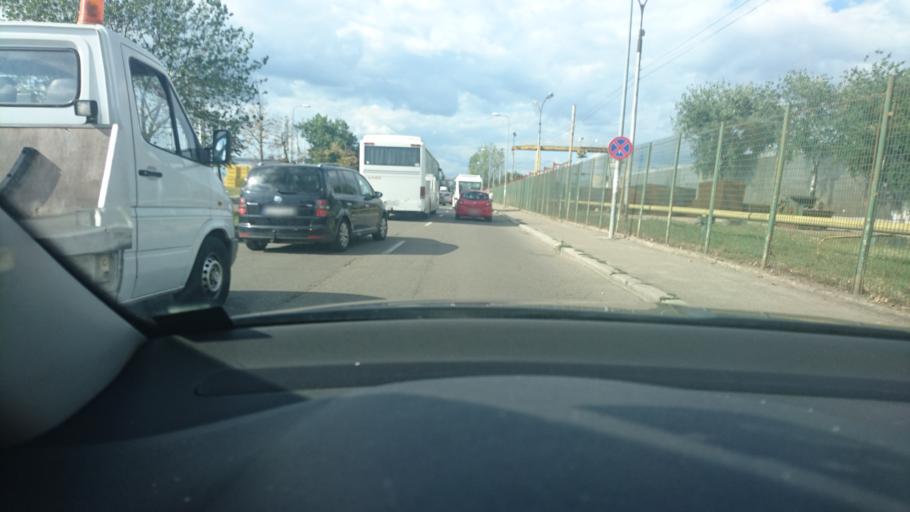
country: RO
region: Buzau
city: Buzau
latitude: 45.1344
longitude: 26.8158
